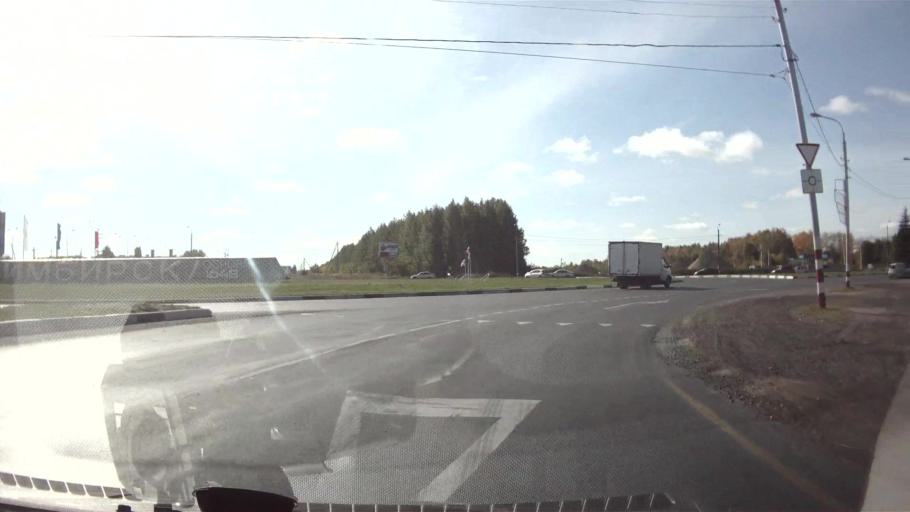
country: RU
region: Ulyanovsk
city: Isheyevka
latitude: 54.2915
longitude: 48.2539
